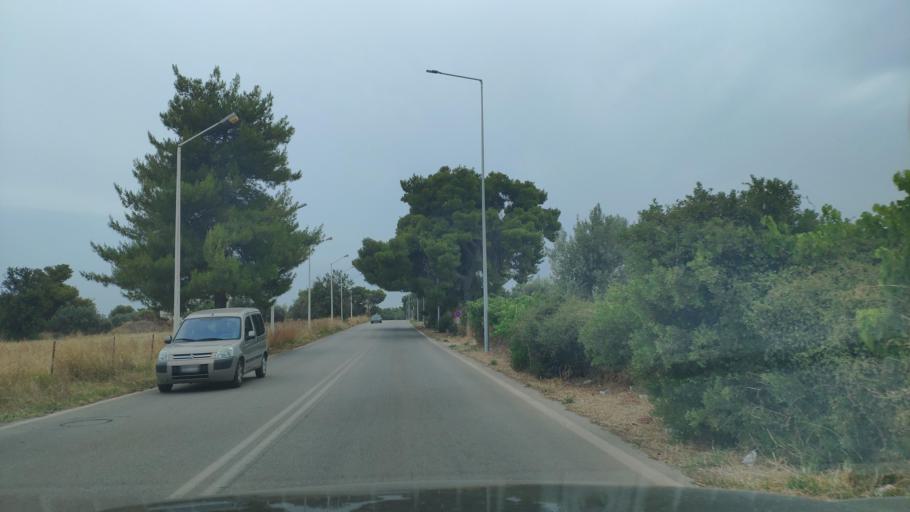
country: GR
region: Peloponnese
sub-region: Nomos Argolidos
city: Porto Cheli
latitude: 37.3411
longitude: 23.1569
